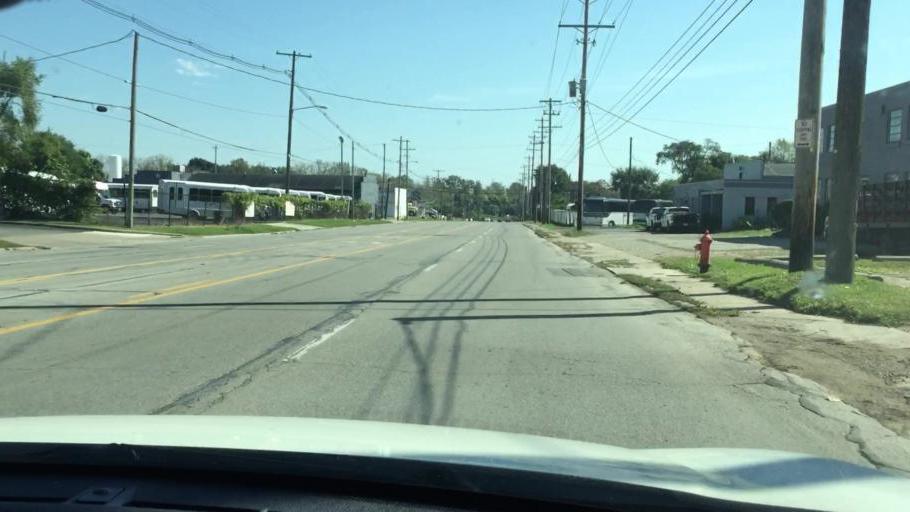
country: US
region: Ohio
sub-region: Franklin County
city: Bexley
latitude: 39.9853
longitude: -82.9621
